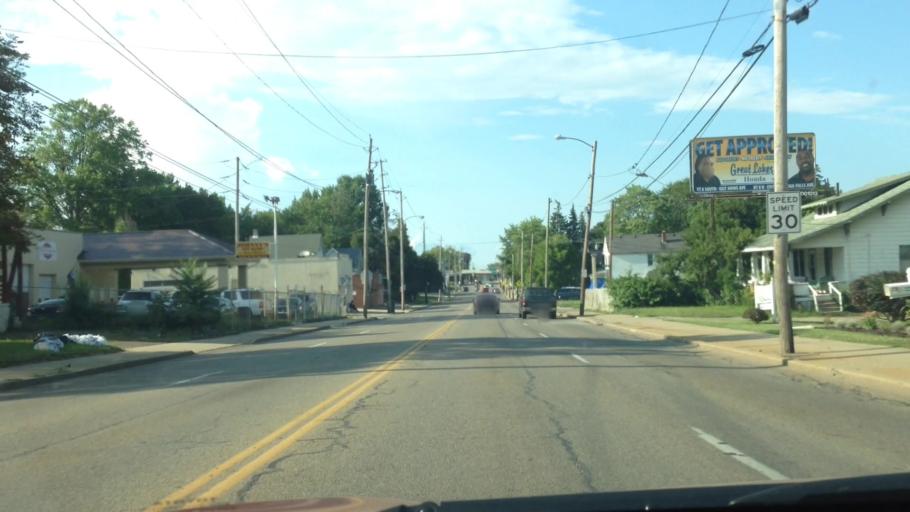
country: US
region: Ohio
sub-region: Summit County
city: Akron
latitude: 41.0587
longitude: -81.4909
